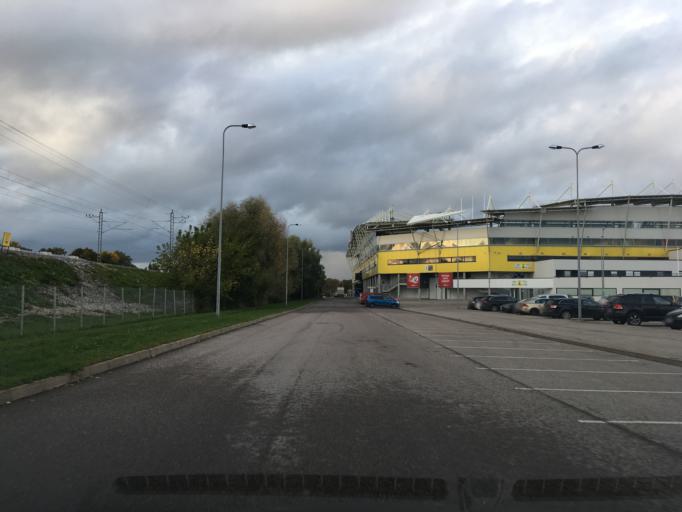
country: EE
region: Harju
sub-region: Tallinna linn
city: Tallinn
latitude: 59.4195
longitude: 24.7317
